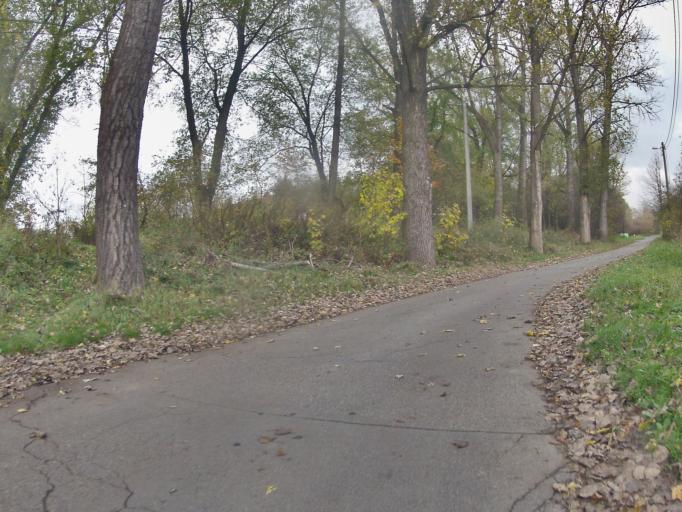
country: PL
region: Lesser Poland Voivodeship
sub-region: Powiat wielicki
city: Wegrzce Wielkie
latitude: 50.0469
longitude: 20.0996
